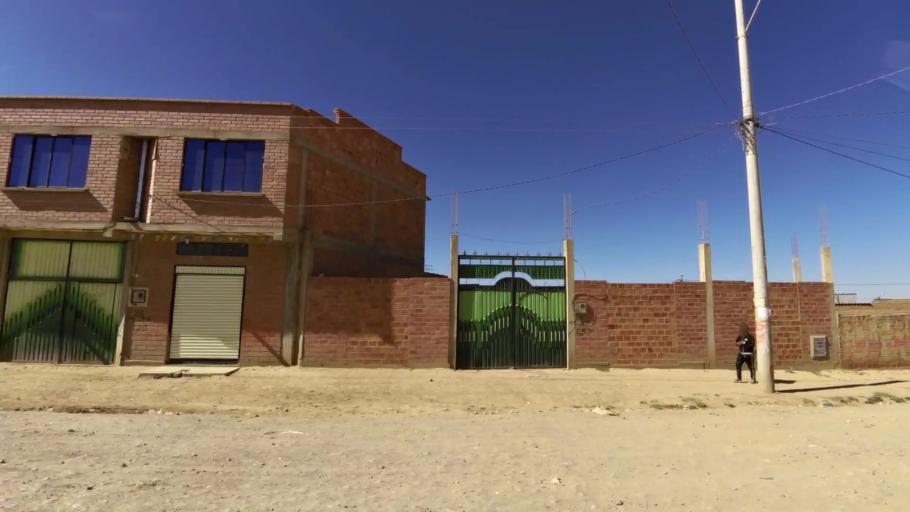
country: BO
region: La Paz
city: La Paz
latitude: -16.6233
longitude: -68.1892
